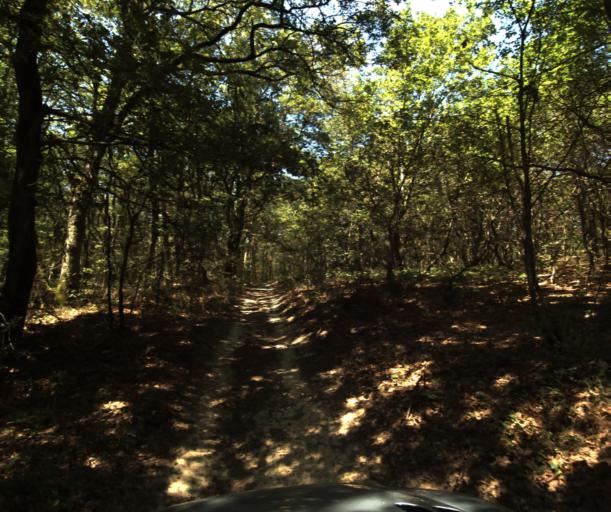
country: FR
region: Midi-Pyrenees
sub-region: Departement de la Haute-Garonne
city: Eaunes
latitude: 43.4088
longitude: 1.3409
